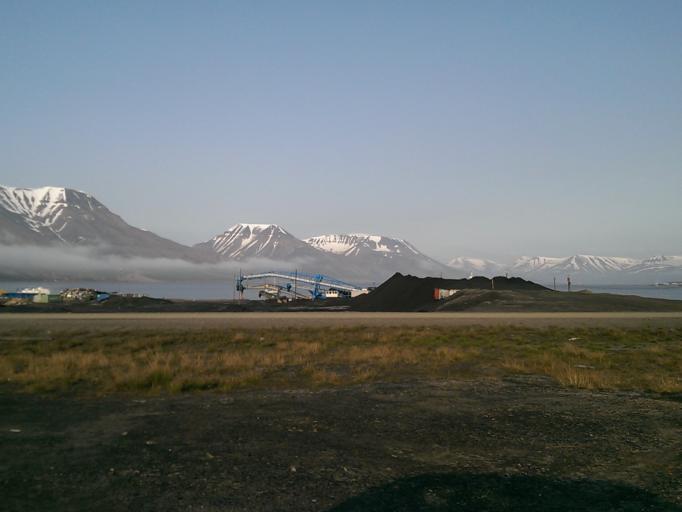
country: SJ
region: Svalbard
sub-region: Spitsbergen
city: Longyearbyen
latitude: 78.2440
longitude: 15.5315
